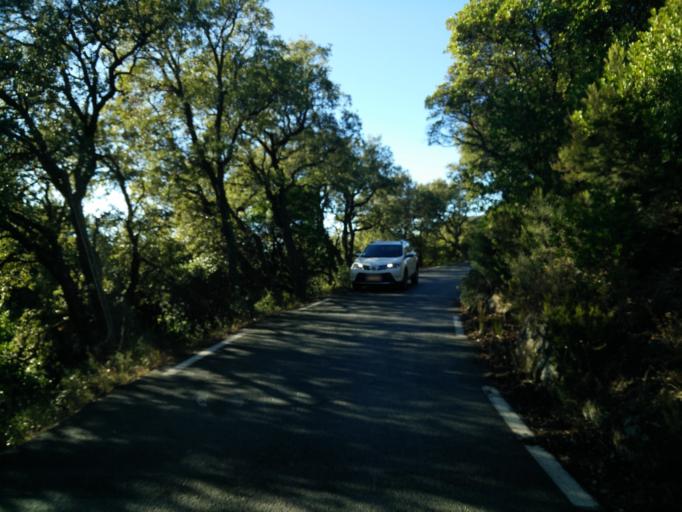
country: FR
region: Provence-Alpes-Cote d'Azur
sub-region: Departement du Var
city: Collobrieres
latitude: 43.2503
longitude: 6.3901
